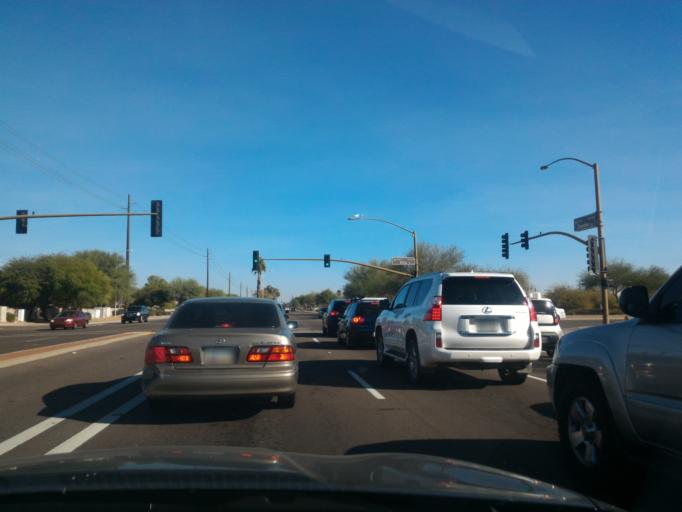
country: US
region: Arizona
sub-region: Maricopa County
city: Chandler
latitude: 33.3059
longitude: -111.8858
